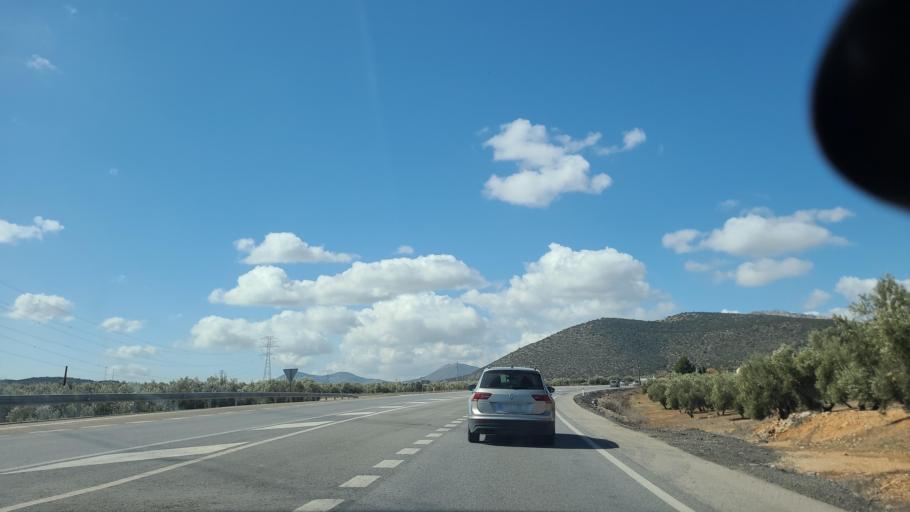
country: ES
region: Andalusia
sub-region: Provincia de Granada
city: Iznalloz
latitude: 37.3994
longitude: -3.5502
